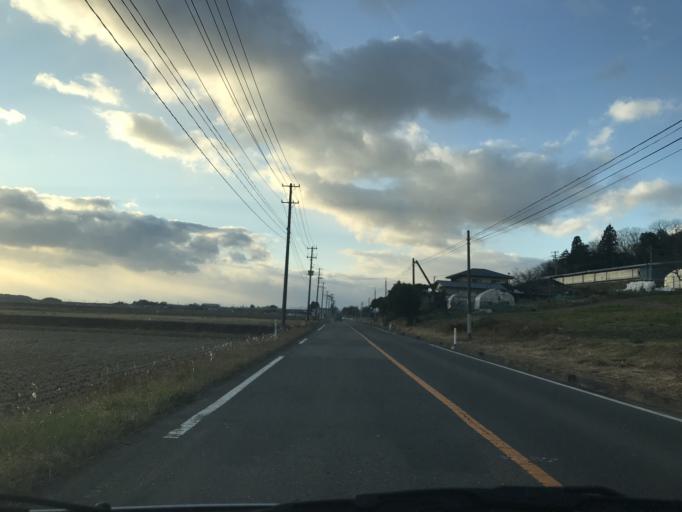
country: JP
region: Miyagi
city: Kogota
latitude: 38.6560
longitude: 141.0364
